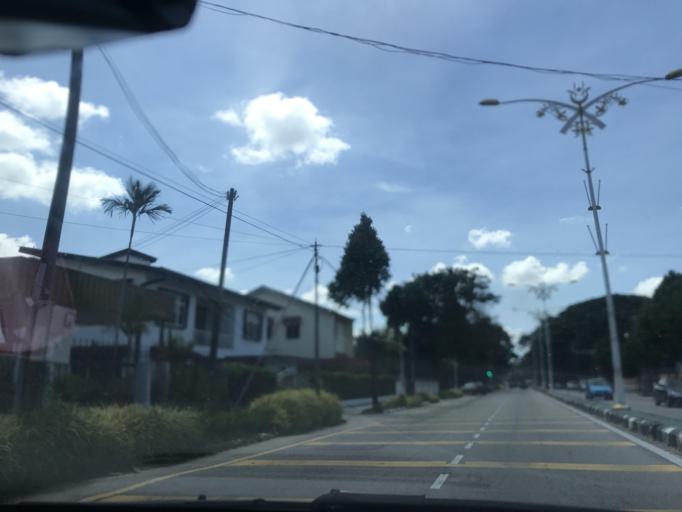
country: MY
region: Kelantan
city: Kota Bharu
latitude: 6.1084
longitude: 102.2496
